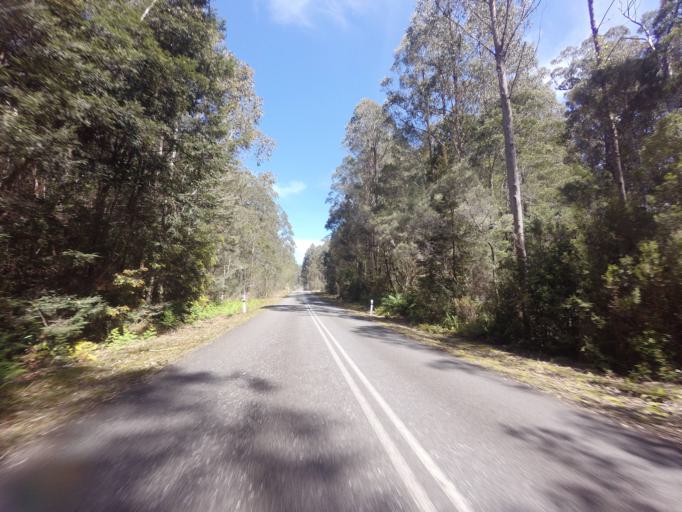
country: AU
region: Tasmania
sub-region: Huon Valley
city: Geeveston
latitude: -42.8364
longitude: 146.2655
